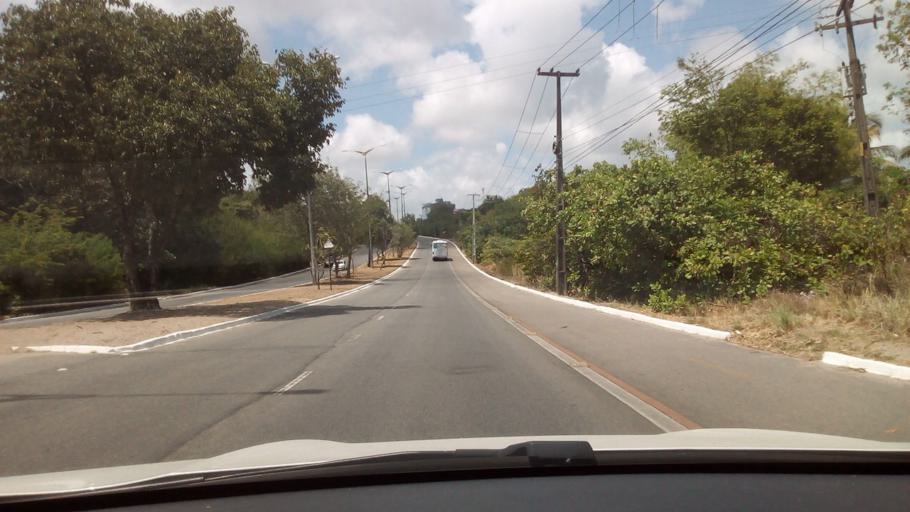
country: BR
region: Paraiba
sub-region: Joao Pessoa
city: Joao Pessoa
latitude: -7.1604
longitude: -34.8129
